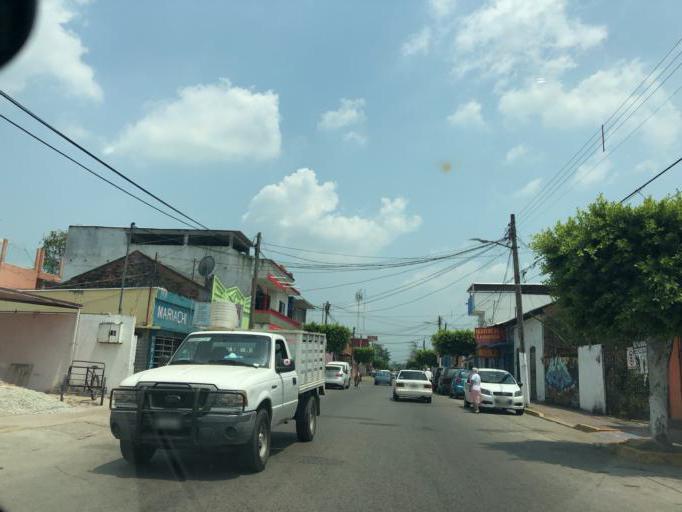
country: MX
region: Tabasco
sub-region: Cardenas
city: Cardenas
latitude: 17.9858
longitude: -93.3769
